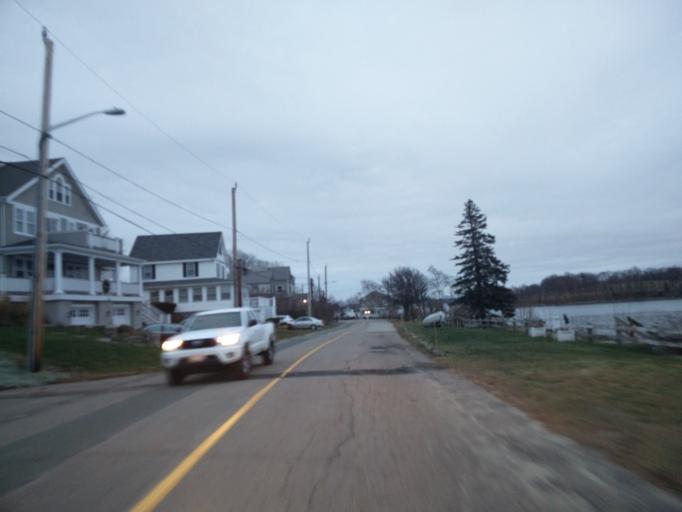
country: US
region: Massachusetts
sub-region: Plymouth County
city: Hull
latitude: 42.2766
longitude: -70.8864
